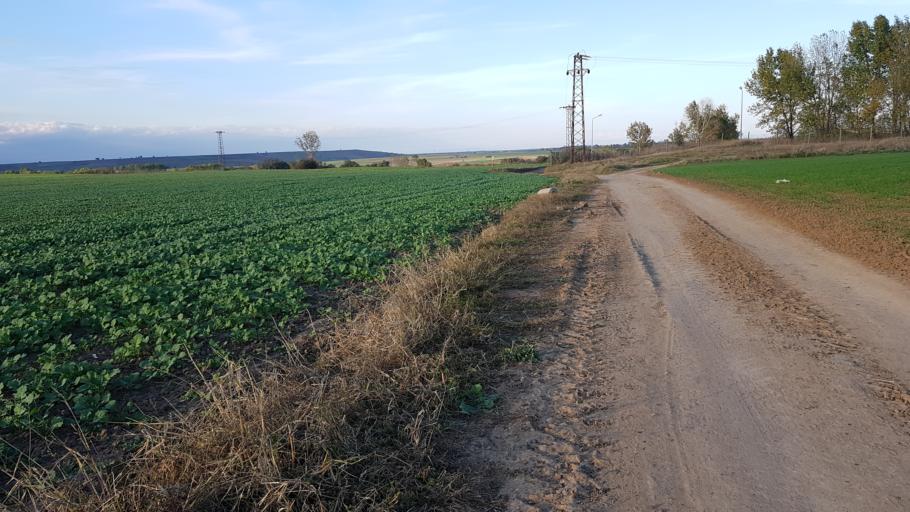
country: TR
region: Tekirdag
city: Muratli
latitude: 41.1906
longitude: 27.4998
